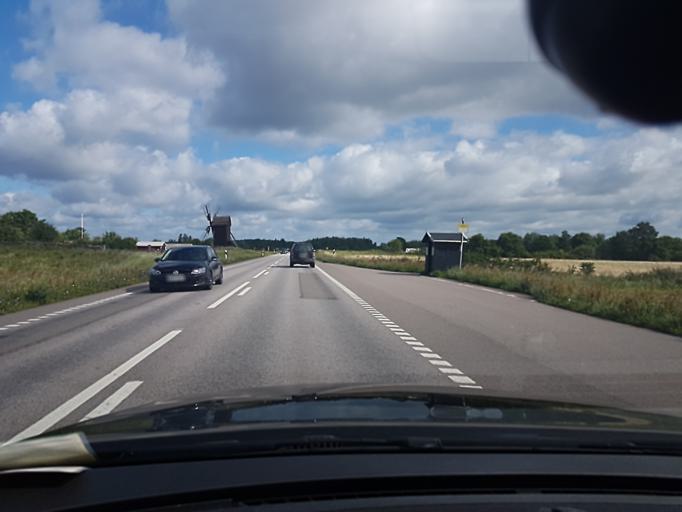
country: SE
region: Kalmar
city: Faerjestaden
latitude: 56.7400
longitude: 16.5459
